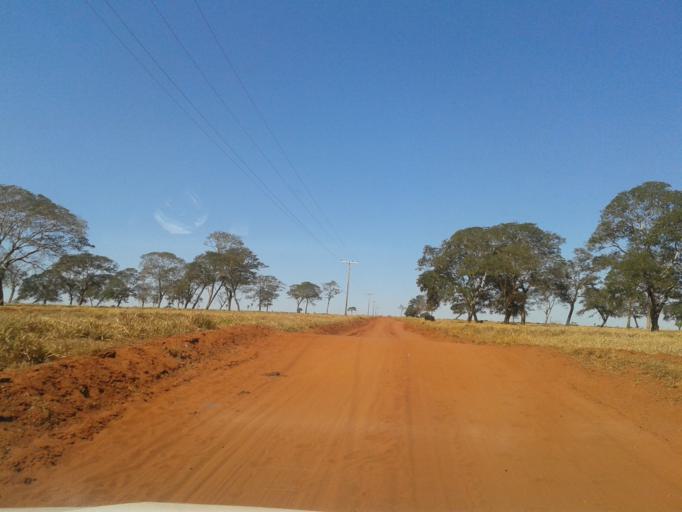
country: BR
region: Minas Gerais
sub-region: Santa Vitoria
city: Santa Vitoria
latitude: -19.2240
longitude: -50.2128
